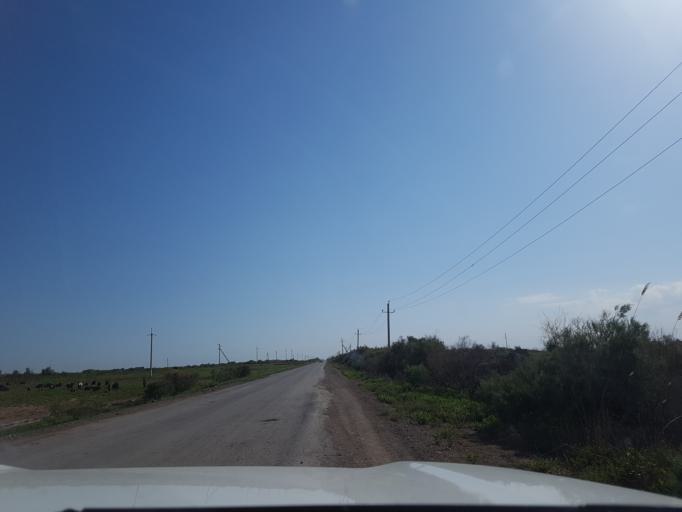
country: TM
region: Dasoguz
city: Koeneuergench
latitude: 42.0849
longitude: 58.8801
